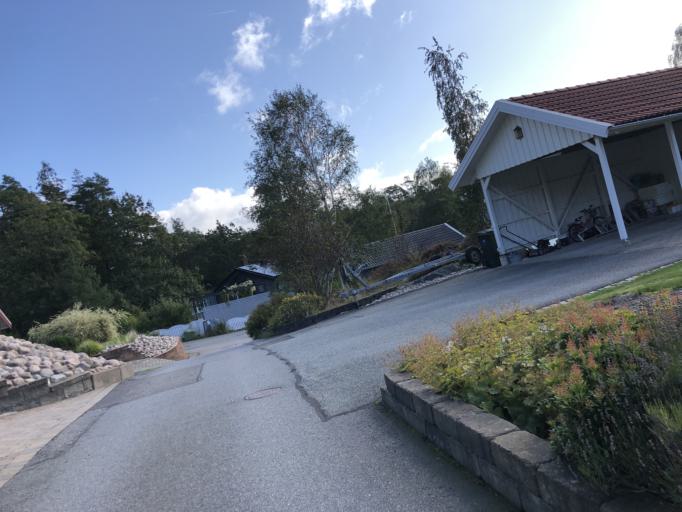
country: SE
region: Vaestra Goetaland
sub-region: Goteborg
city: Torslanda
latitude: 57.7472
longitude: 11.8202
